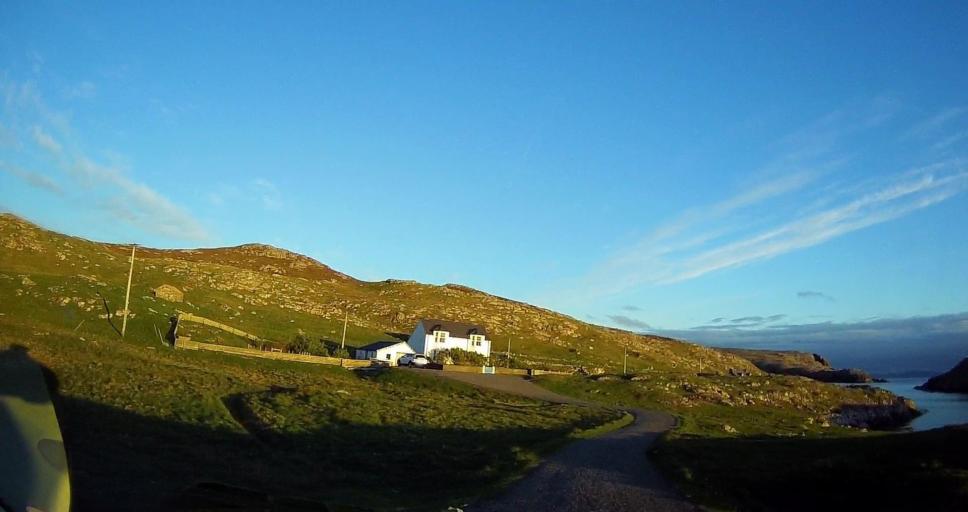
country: GB
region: Scotland
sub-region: Shetland Islands
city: Lerwick
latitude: 60.4418
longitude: -1.4477
